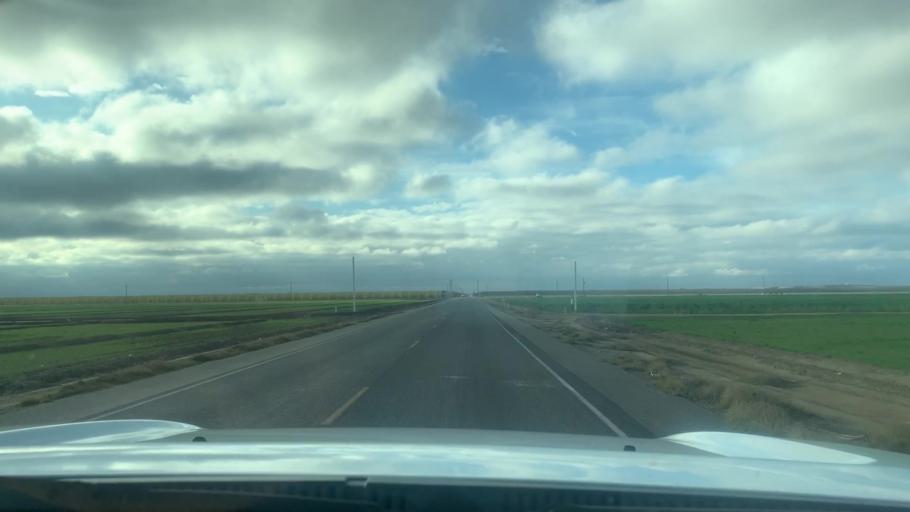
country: US
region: California
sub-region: Kern County
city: Wasco
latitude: 35.5001
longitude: -119.3806
